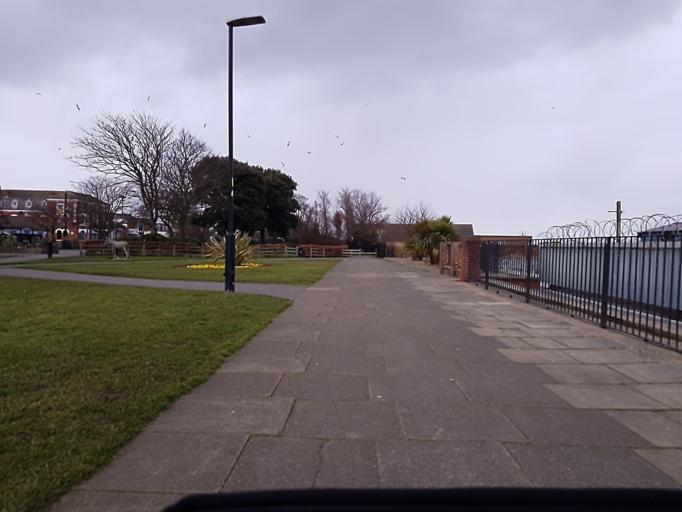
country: GB
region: England
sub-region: North East Lincolnshire
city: Cleethorpes
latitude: 53.5599
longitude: -0.0272
